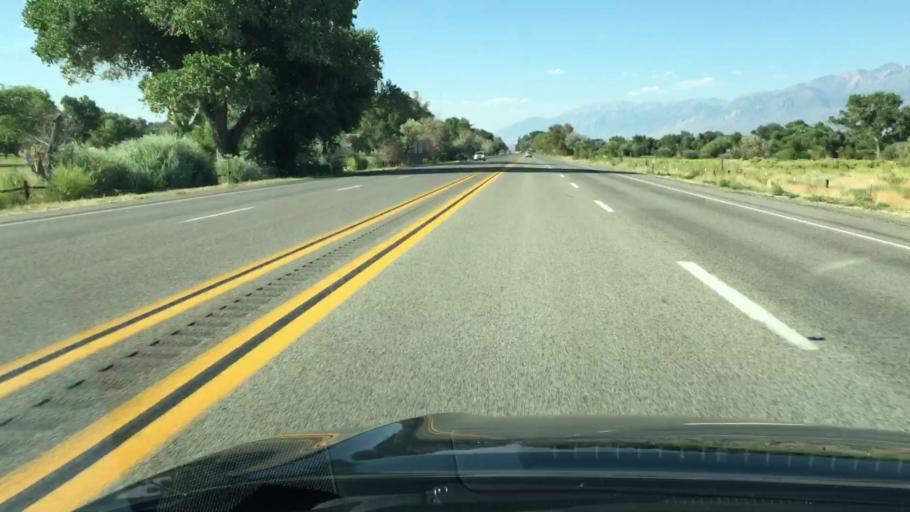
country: US
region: California
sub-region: Inyo County
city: Bishop
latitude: 37.3373
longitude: -118.3954
